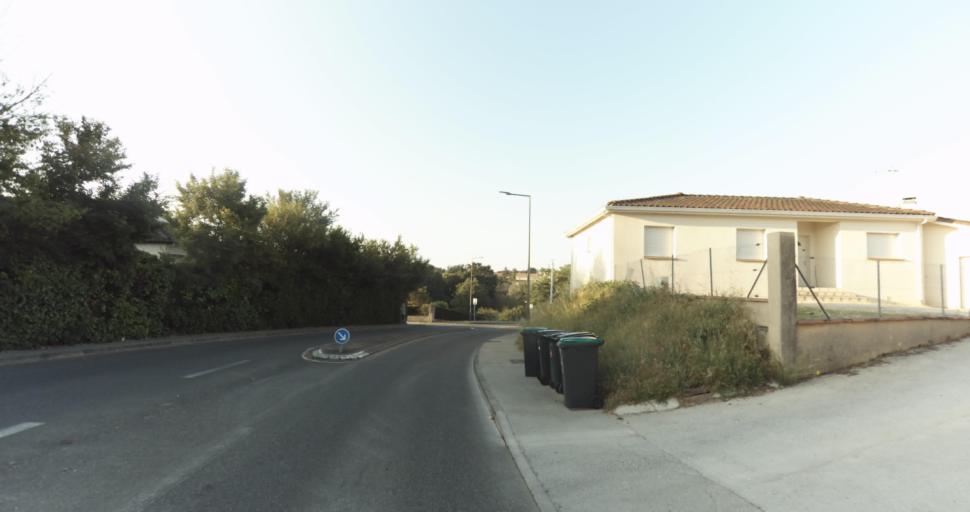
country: FR
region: Midi-Pyrenees
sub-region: Departement de la Haute-Garonne
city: Leguevin
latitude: 43.5970
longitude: 1.2314
